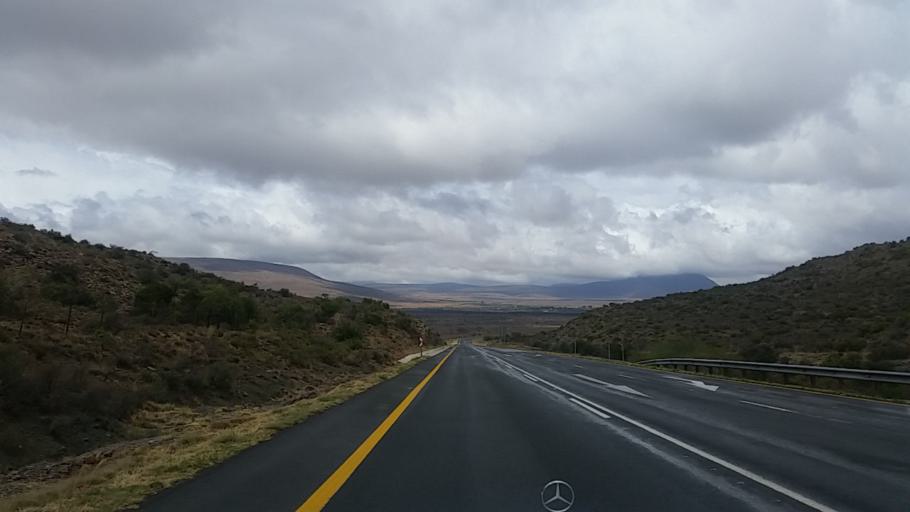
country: ZA
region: Eastern Cape
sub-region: Cacadu District Municipality
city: Graaff-Reinet
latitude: -32.1414
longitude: 24.5768
